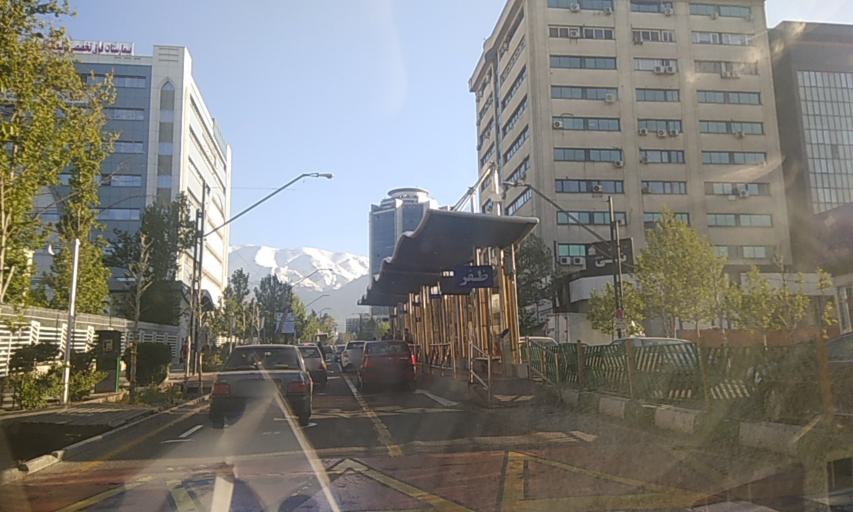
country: IR
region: Tehran
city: Tajrish
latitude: 35.7671
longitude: 51.4110
